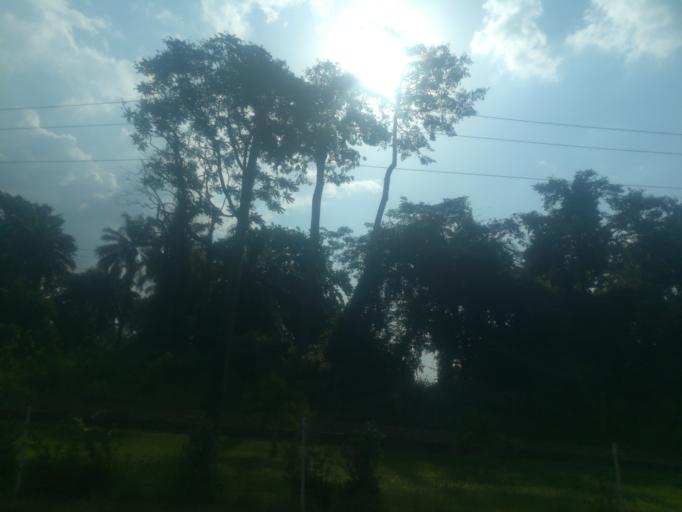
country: NG
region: Oyo
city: Moniya
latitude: 7.4968
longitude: 3.9138
